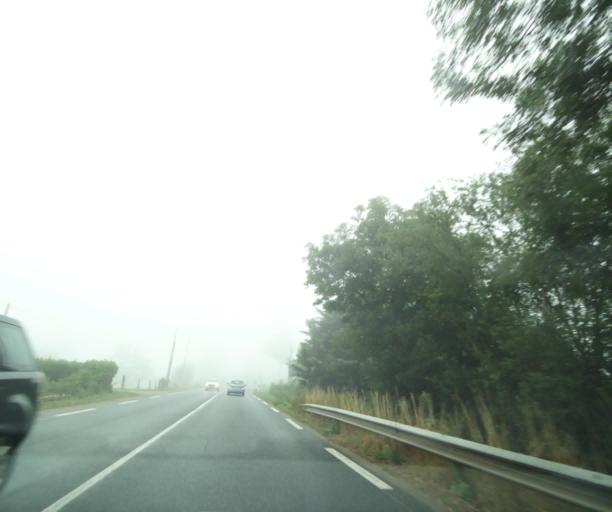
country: FR
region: Midi-Pyrenees
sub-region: Departement de l'Aveyron
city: Baraqueville
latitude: 44.2558
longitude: 2.4150
